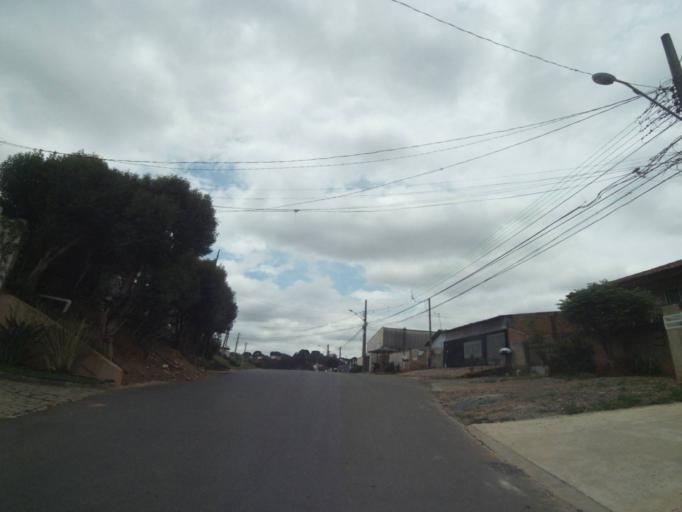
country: BR
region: Parana
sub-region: Curitiba
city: Curitiba
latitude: -25.3877
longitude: -49.2943
